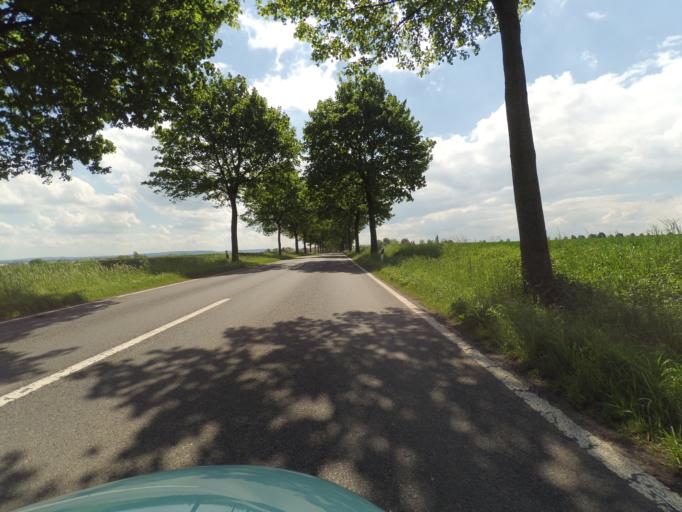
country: DE
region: Lower Saxony
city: Hohenhameln
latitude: 52.2081
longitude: 10.0370
